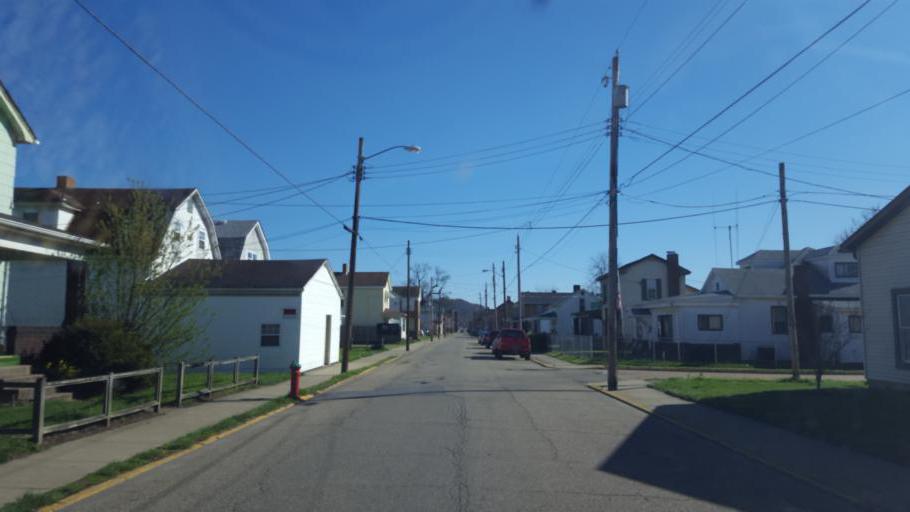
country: US
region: Ohio
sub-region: Jefferson County
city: Toronto
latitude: 40.4699
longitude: -80.6008
